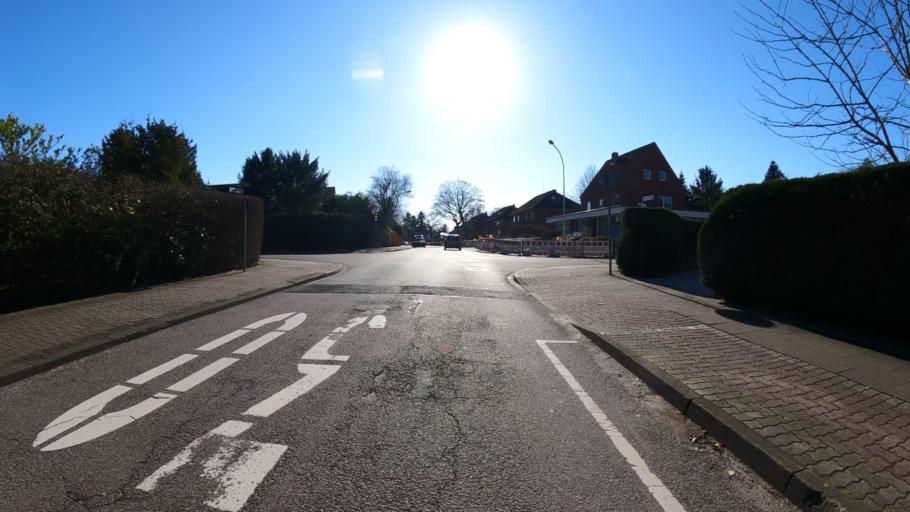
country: DE
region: Schleswig-Holstein
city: Rellingen
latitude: 53.6480
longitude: 9.7977
